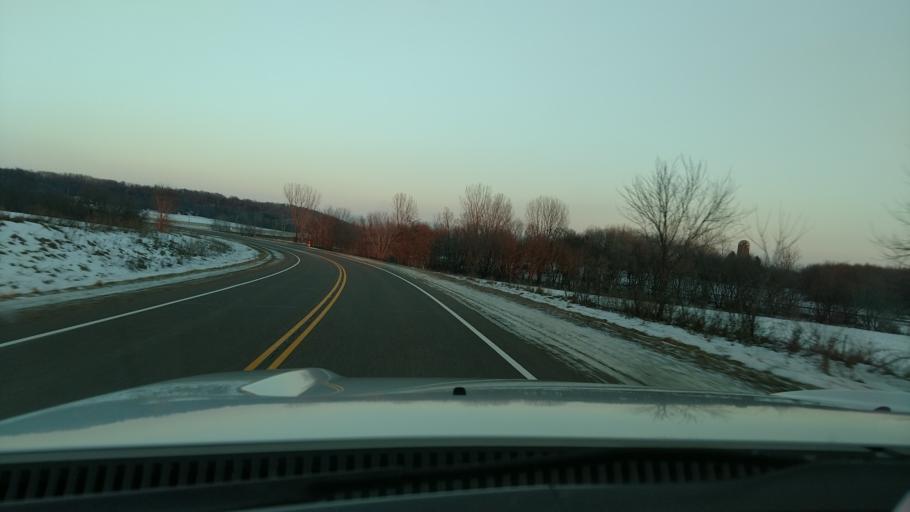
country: US
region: Wisconsin
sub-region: Pierce County
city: River Falls
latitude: 44.9062
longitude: -92.5615
